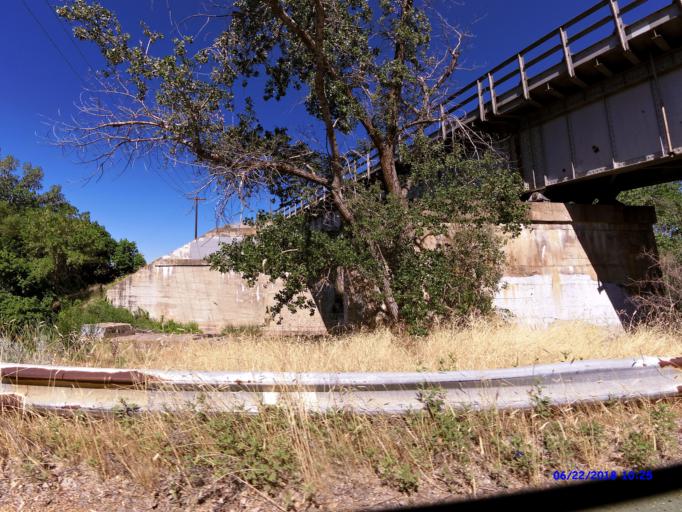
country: US
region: Utah
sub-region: Weber County
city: South Ogden
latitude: 41.2038
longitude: -111.9910
